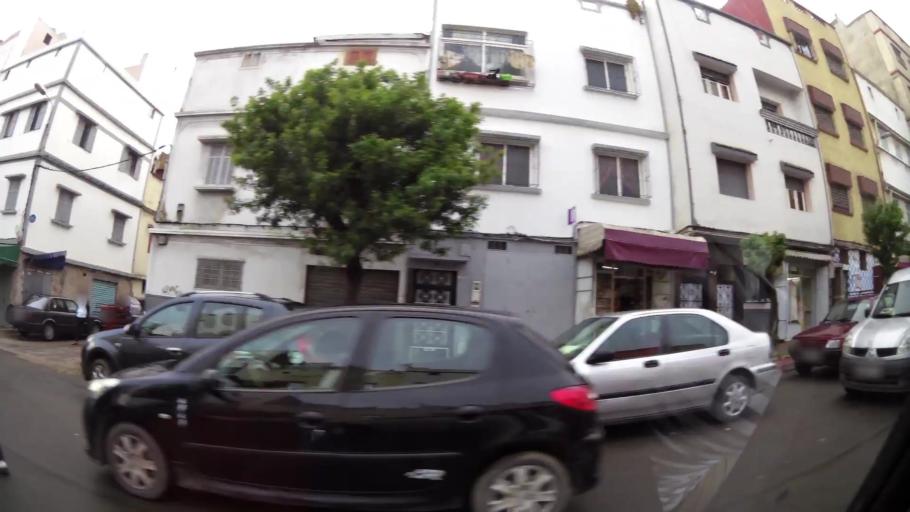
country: MA
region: Grand Casablanca
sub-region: Casablanca
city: Casablanca
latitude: 33.5504
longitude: -7.5763
